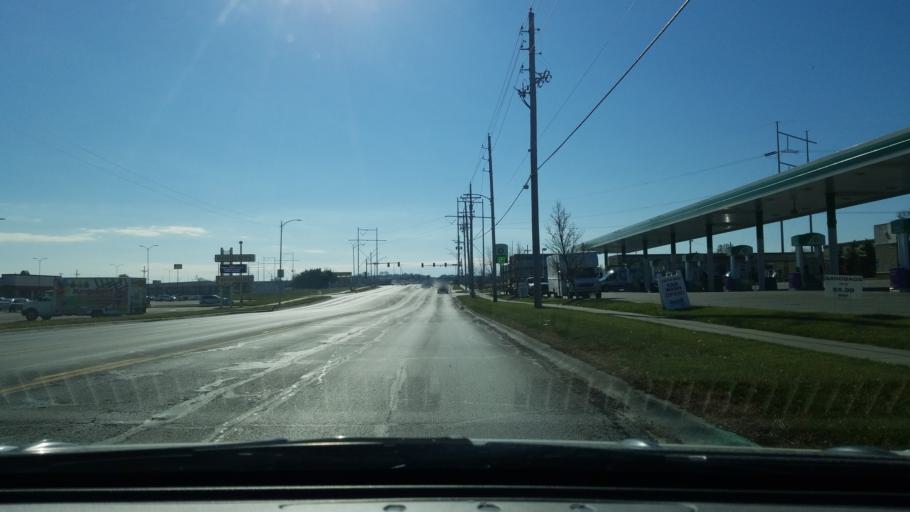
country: US
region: Nebraska
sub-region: Douglas County
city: Ralston
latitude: 41.2296
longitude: -96.0431
